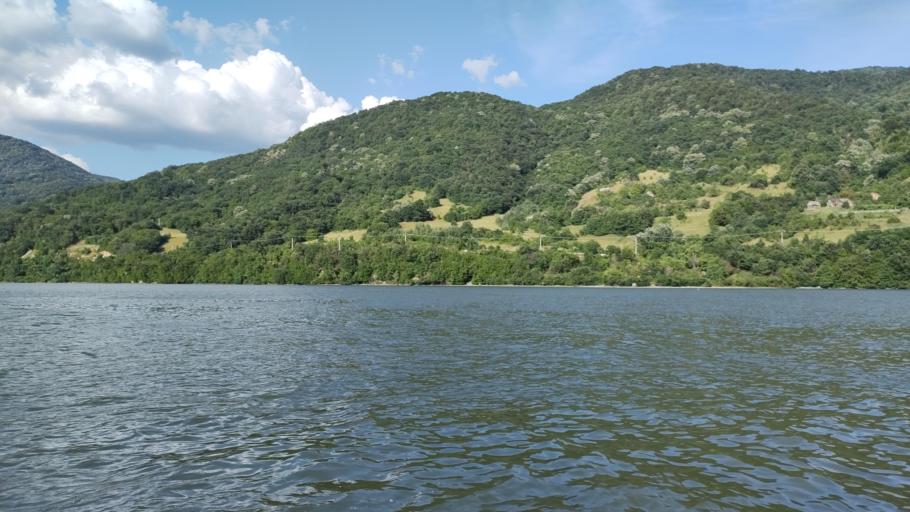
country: RO
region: Caras-Severin
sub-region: Comuna Berzasca
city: Berzasca
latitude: 44.5721
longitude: 22.0282
